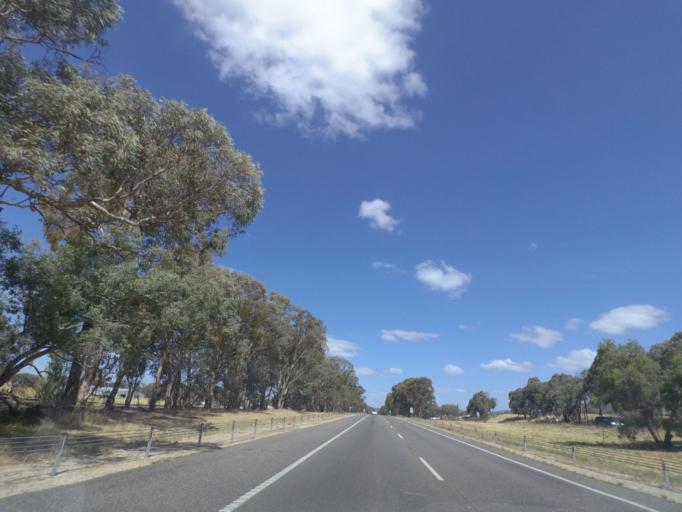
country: AU
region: Victoria
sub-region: Wodonga
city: Wodonga
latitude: -36.0959
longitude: 146.8151
